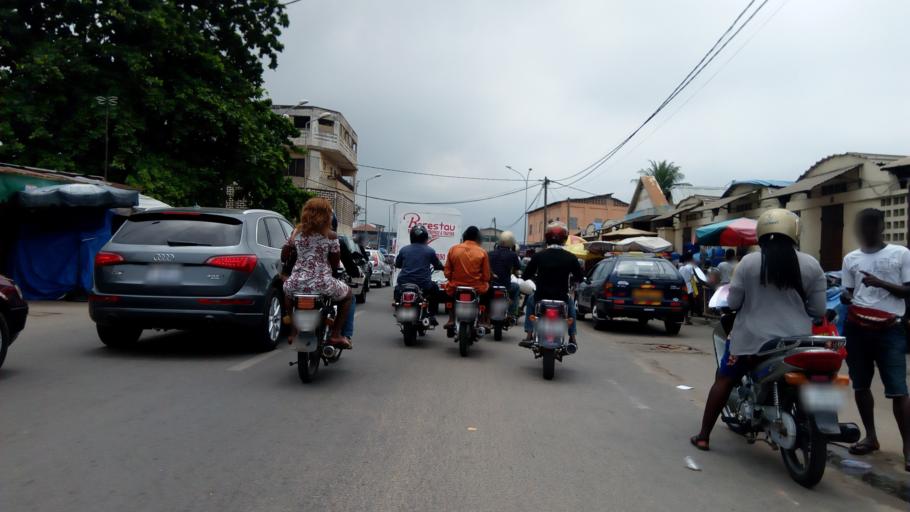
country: TG
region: Maritime
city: Lome
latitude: 6.1411
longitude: 1.2297
